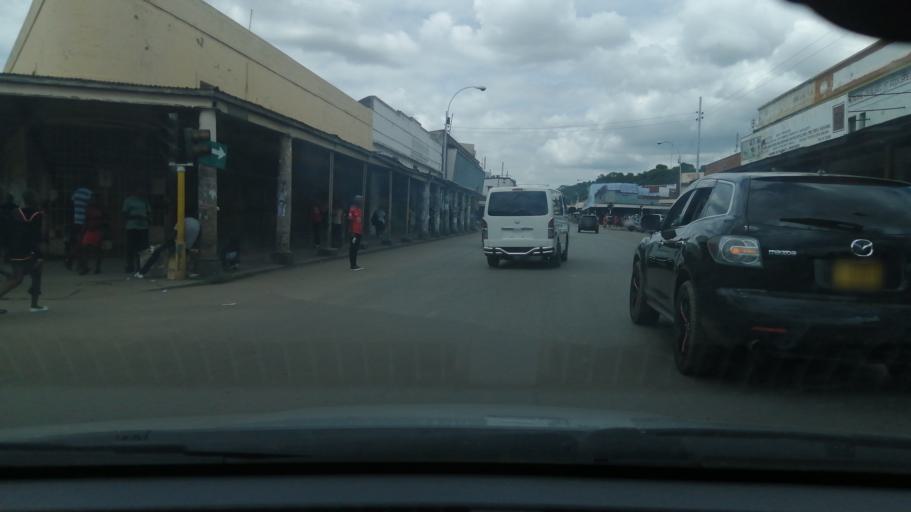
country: ZW
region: Harare
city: Harare
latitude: -17.8371
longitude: 31.0449
